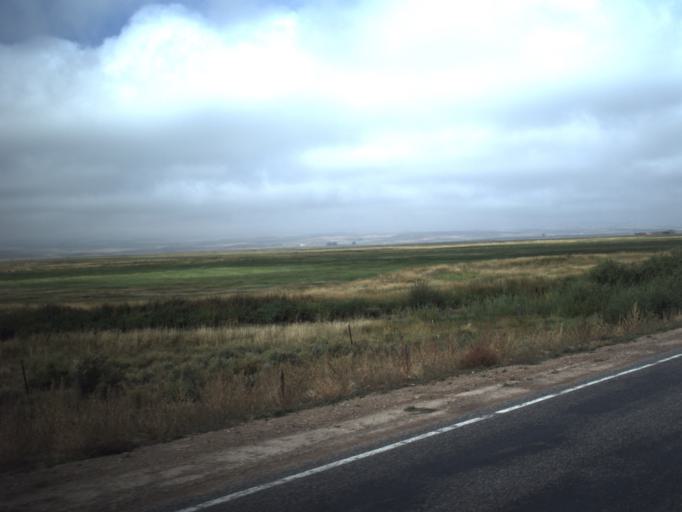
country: US
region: Utah
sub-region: Rich County
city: Randolph
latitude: 41.4687
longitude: -111.1056
